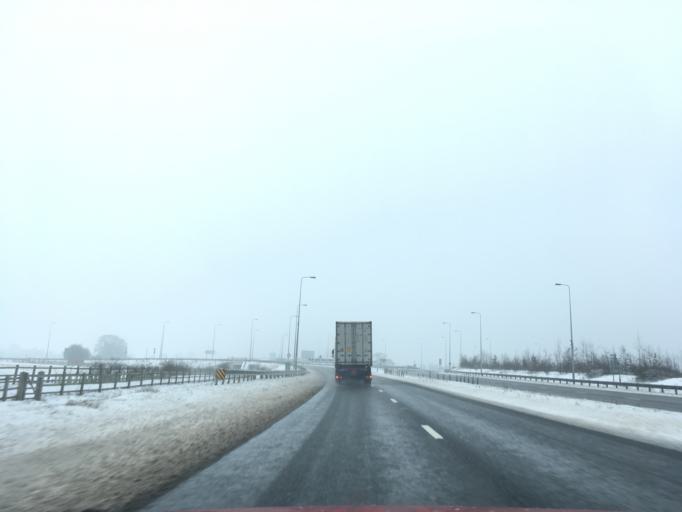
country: GB
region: England
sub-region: Warwickshire
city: Warwick
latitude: 52.2575
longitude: -1.6219
